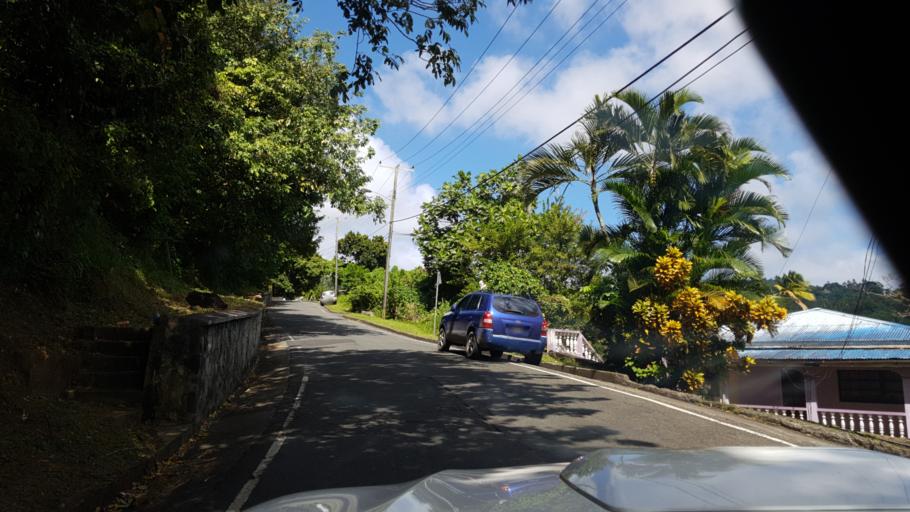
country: LC
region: Castries Quarter
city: Castries
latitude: 13.9847
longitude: -60.9727
